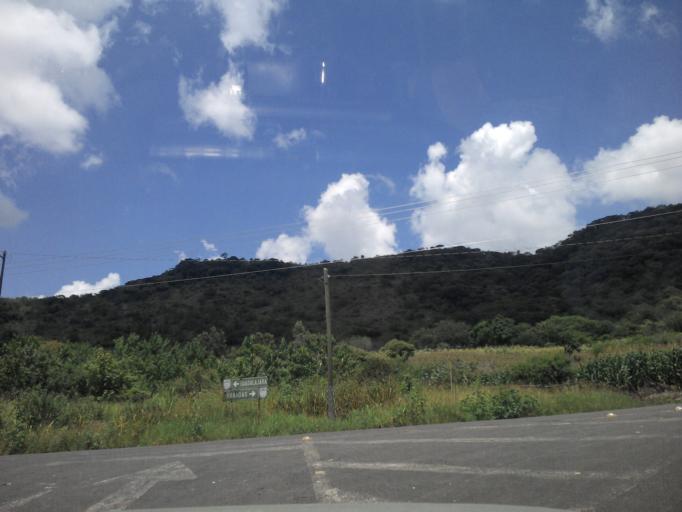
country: MX
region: Jalisco
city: Atotonilco el Alto
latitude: 20.5700
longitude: -102.5148
